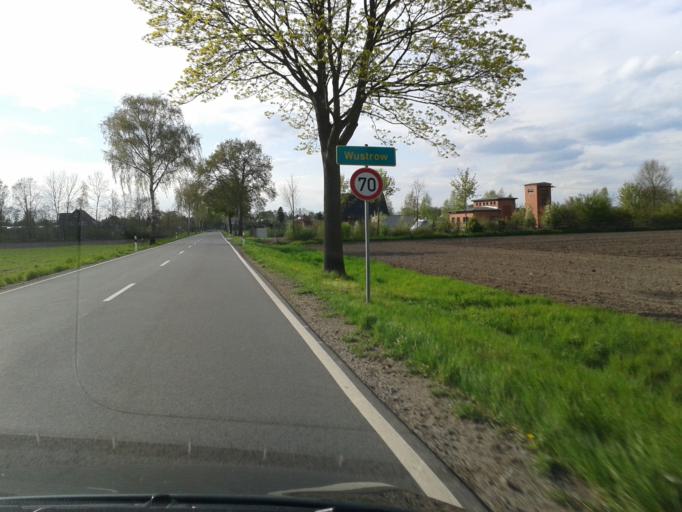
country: DE
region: Lower Saxony
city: Wustrow
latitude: 52.9207
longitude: 11.1397
